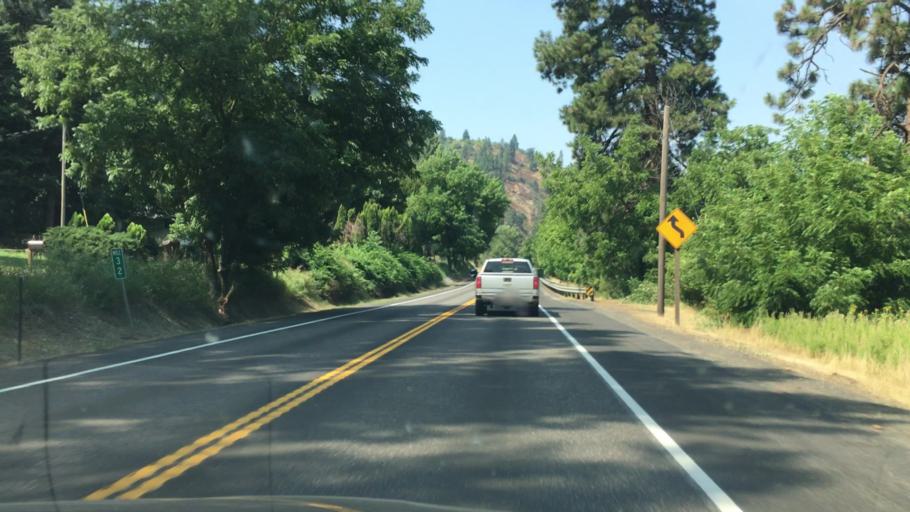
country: US
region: Idaho
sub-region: Clearwater County
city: Orofino
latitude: 46.4999
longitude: -116.4796
